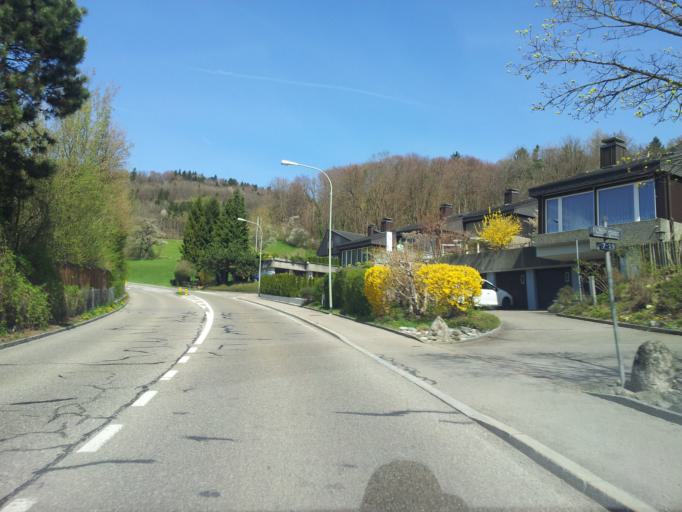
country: CH
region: Zurich
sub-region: Bezirk Dietikon
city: Weiningen
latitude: 47.4221
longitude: 8.4371
